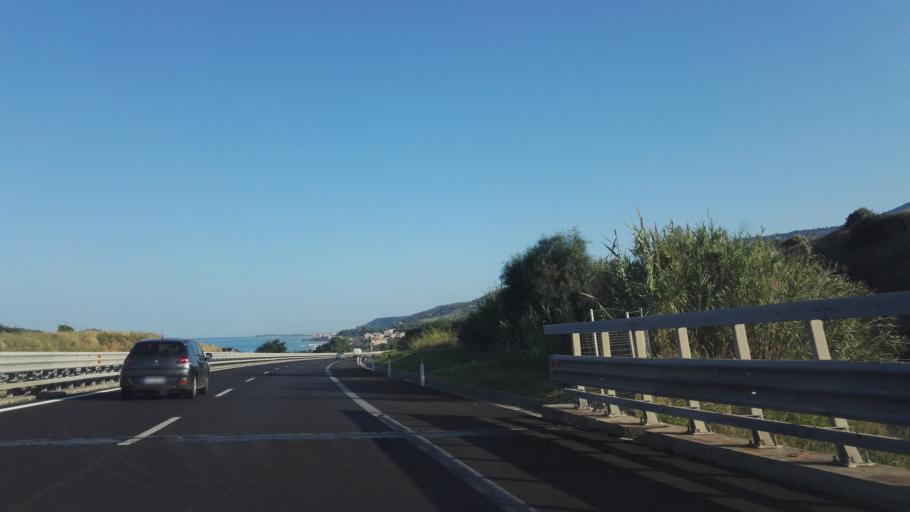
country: IT
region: Calabria
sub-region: Provincia di Catanzaro
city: Falerna Scalo
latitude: 38.9546
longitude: 16.1573
